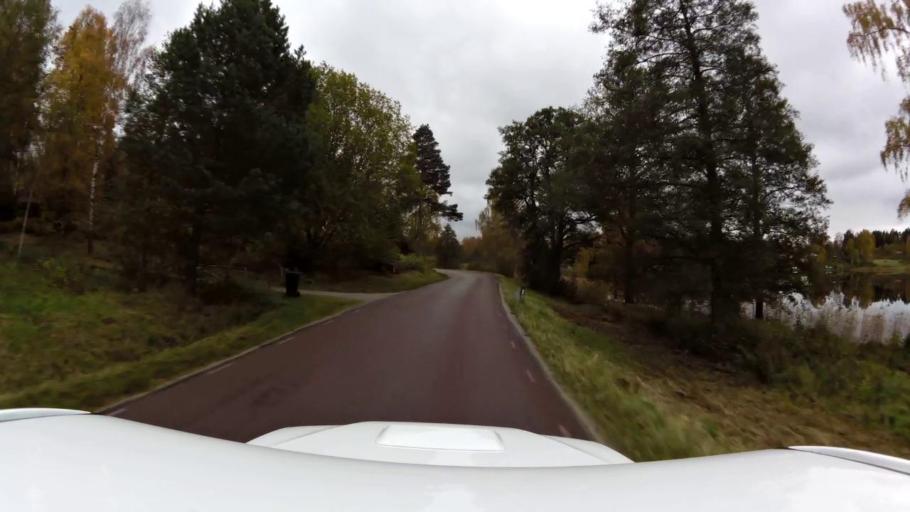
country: SE
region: OEstergoetland
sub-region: Linkopings Kommun
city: Ljungsbro
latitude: 58.5721
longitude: 15.5128
